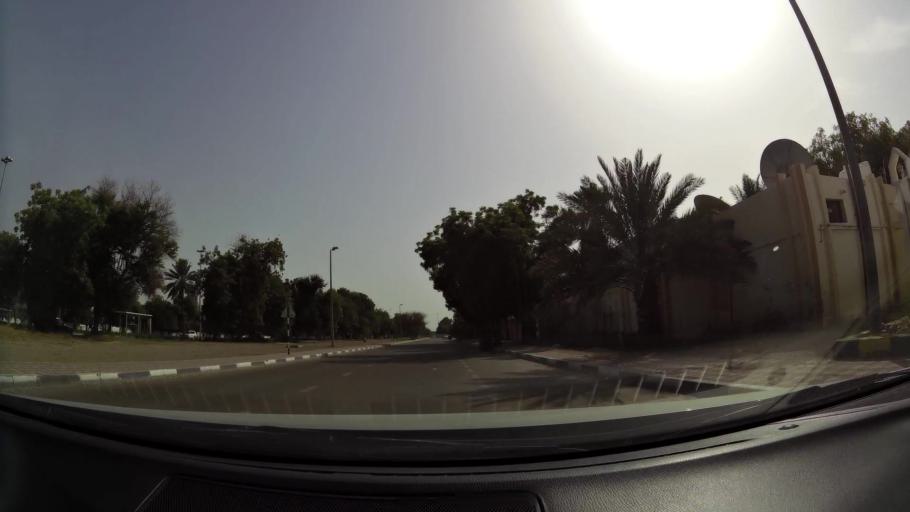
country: AE
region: Abu Dhabi
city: Al Ain
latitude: 24.1632
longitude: 55.7072
